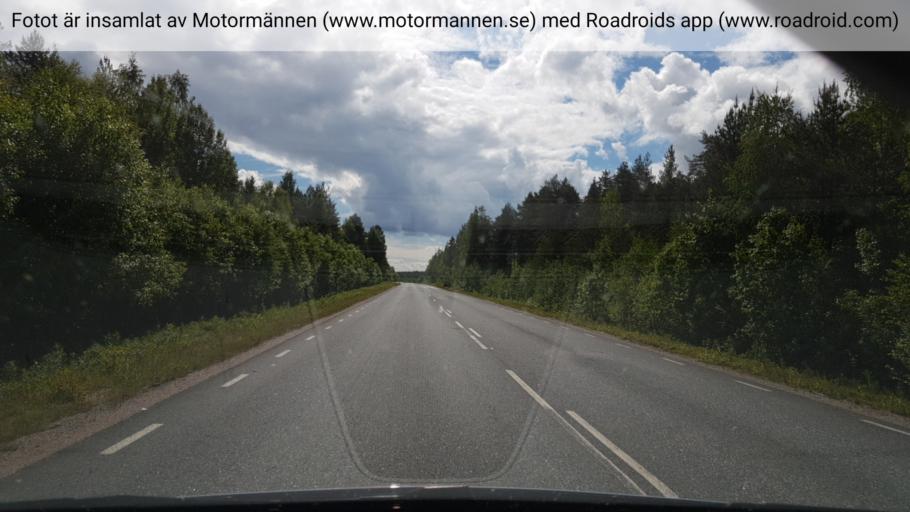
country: FI
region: Lapland
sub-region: Torniolaakso
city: Ylitornio
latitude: 66.3115
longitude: 23.6213
